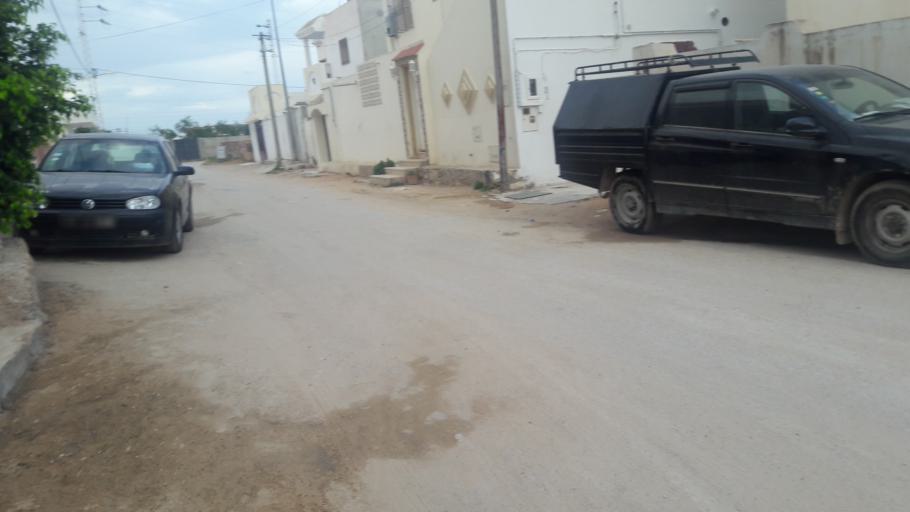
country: TN
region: Safaqis
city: Al Qarmadah
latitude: 34.8102
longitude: 10.7465
